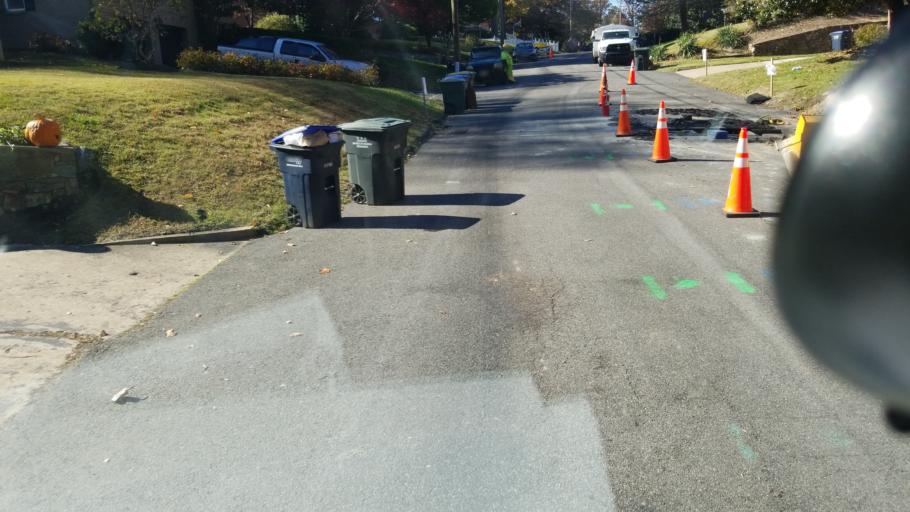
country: US
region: Maryland
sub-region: Montgomery County
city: Chevy Chase
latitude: 38.9805
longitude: -77.0523
